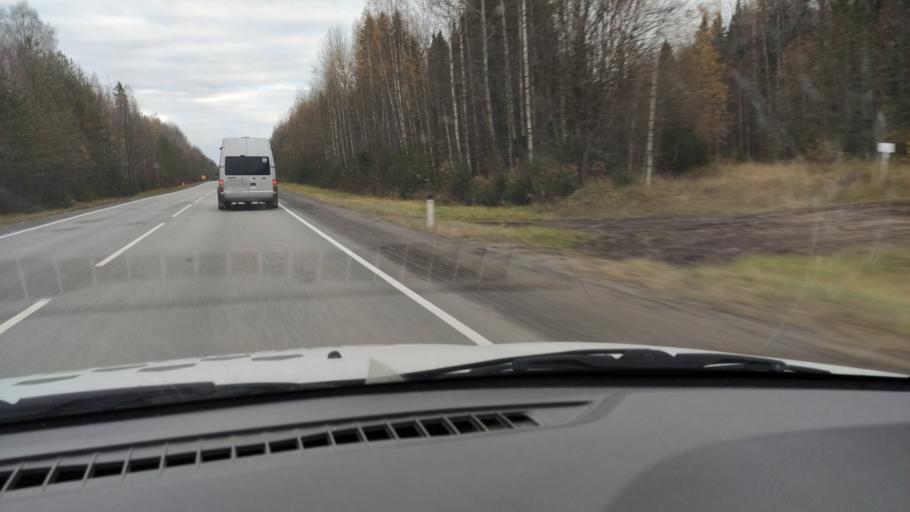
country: RU
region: Kirov
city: Chernaya Kholunitsa
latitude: 58.8587
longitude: 51.6410
